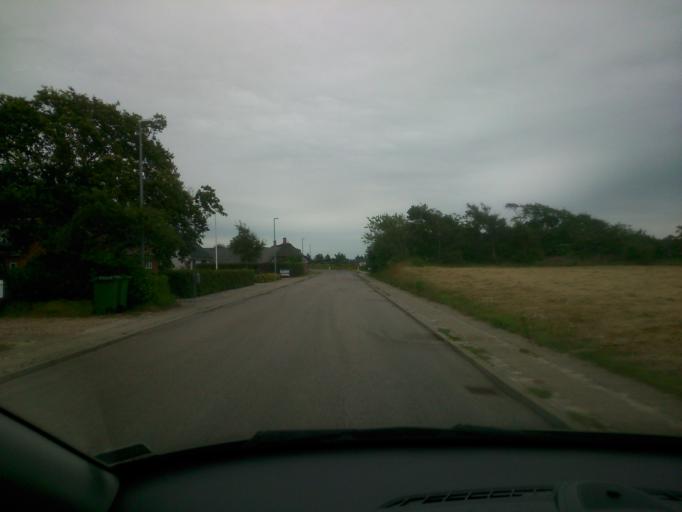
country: DK
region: Central Jutland
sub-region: Ringkobing-Skjern Kommune
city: Skjern
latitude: 55.9596
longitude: 8.3773
